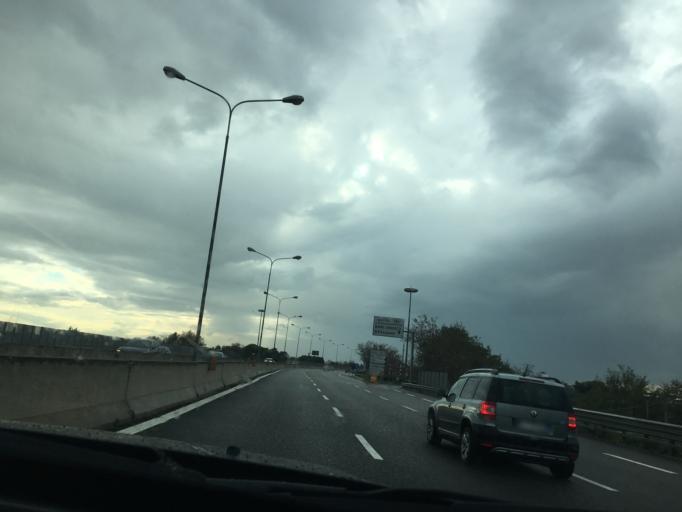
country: IT
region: Apulia
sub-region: Provincia di Bari
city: Triggiano
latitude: 41.0930
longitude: 16.8954
